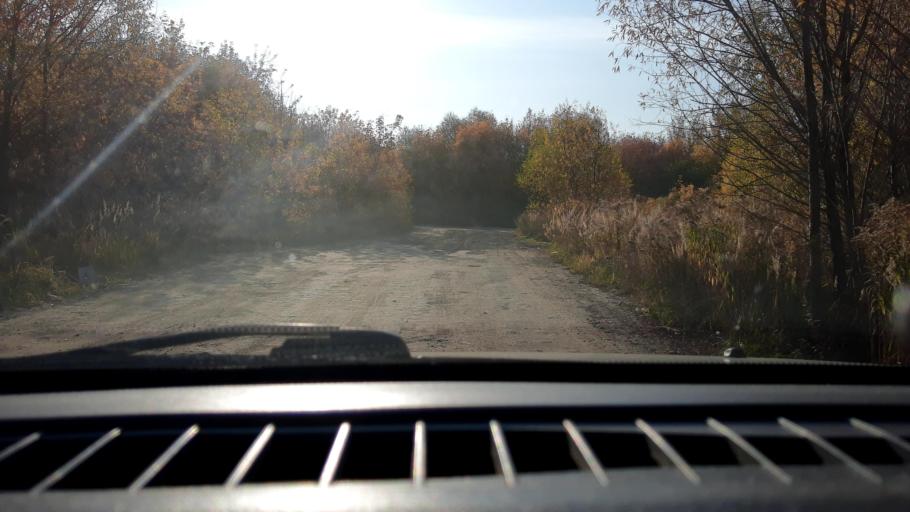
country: RU
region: Nizjnij Novgorod
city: Nizhniy Novgorod
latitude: 56.2501
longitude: 43.9923
